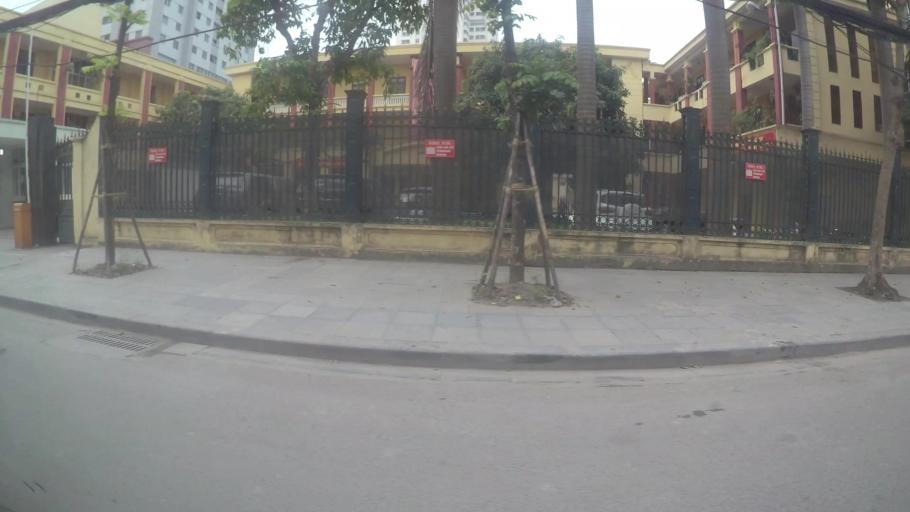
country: VN
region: Ha Noi
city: Ha Dong
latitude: 20.9677
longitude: 105.7700
